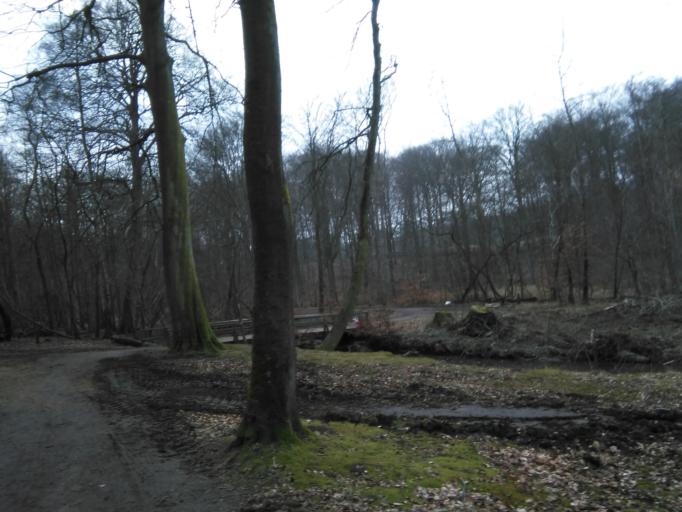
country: DK
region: Central Jutland
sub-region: Arhus Kommune
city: Beder
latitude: 56.0873
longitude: 10.2387
